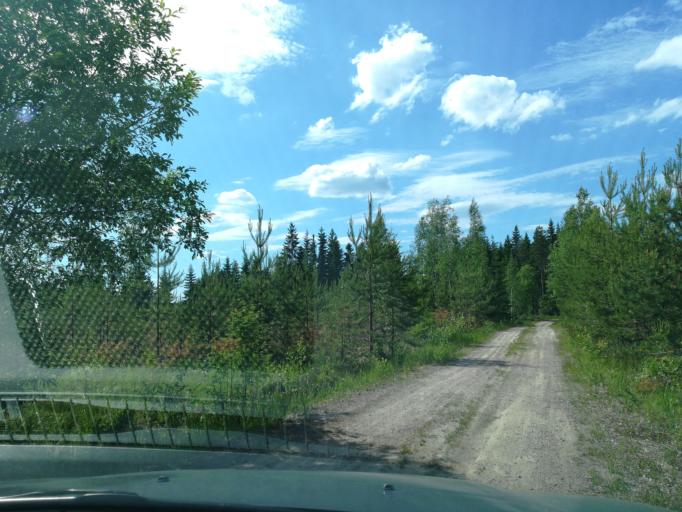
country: FI
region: South Karelia
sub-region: Imatra
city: Ruokolahti
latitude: 61.4772
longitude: 28.8727
